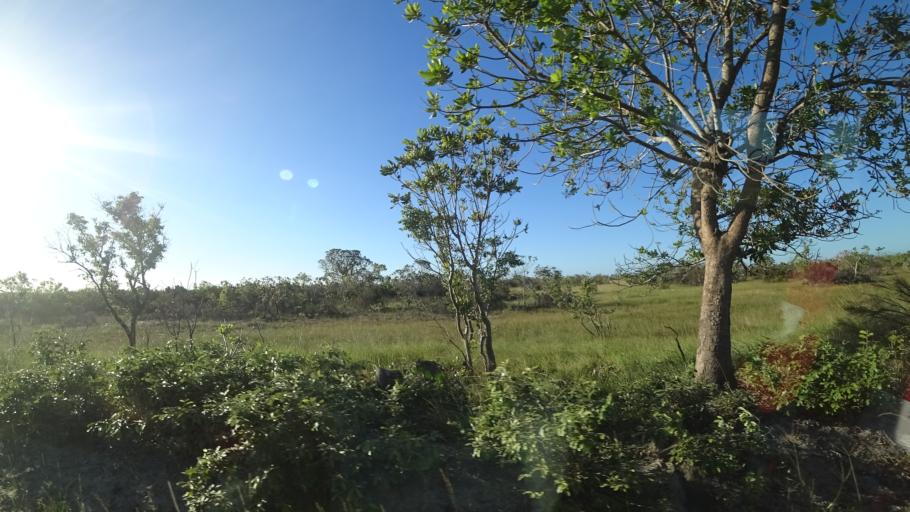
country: MZ
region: Sofala
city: Beira
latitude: -19.5791
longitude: 35.1730
